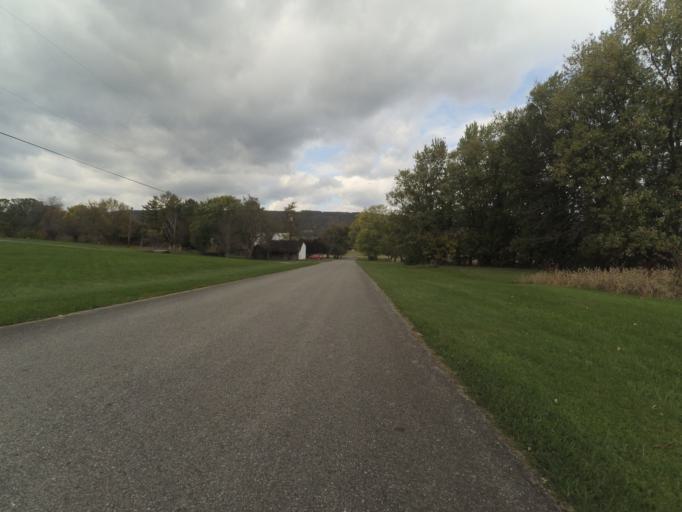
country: US
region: Pennsylvania
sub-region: Centre County
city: Bellefonte
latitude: 40.8904
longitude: -77.8148
